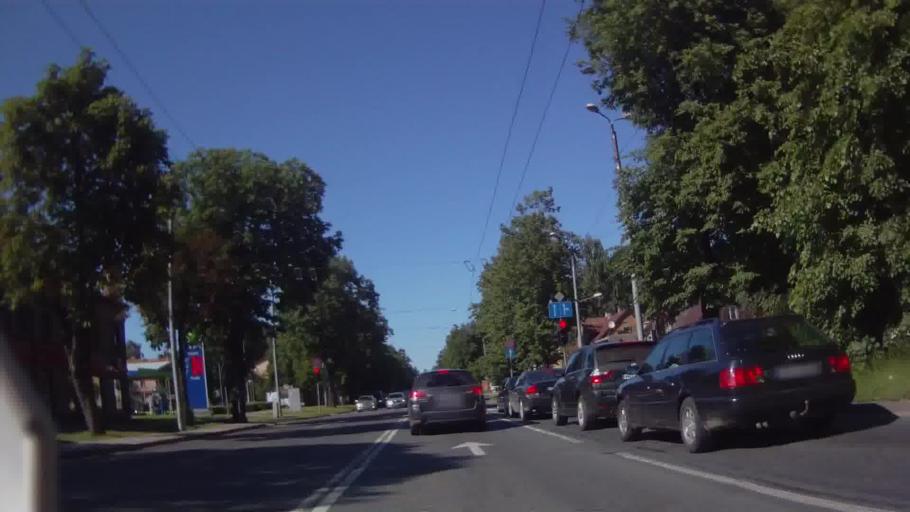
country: LV
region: Riga
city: Riga
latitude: 56.9161
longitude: 24.0877
